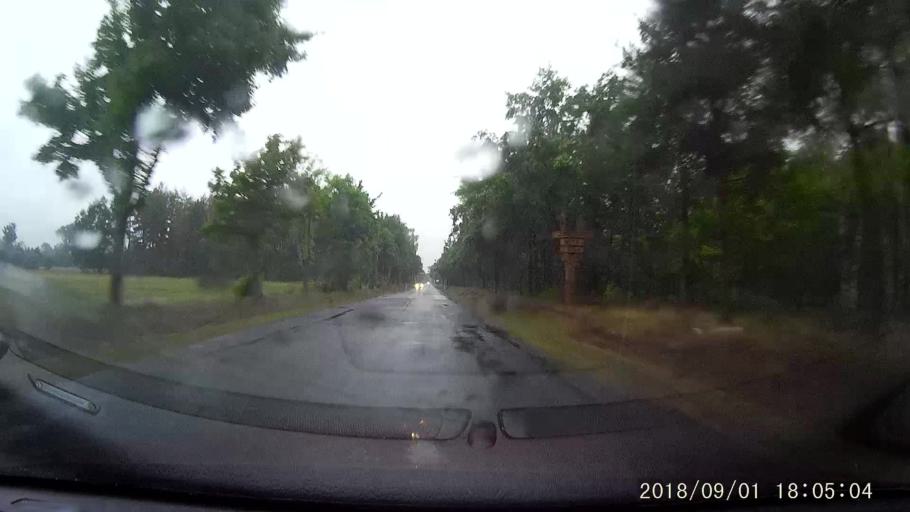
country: PL
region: Lubusz
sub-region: Powiat zaganski
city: Gozdnica
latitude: 51.3655
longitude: 15.1615
